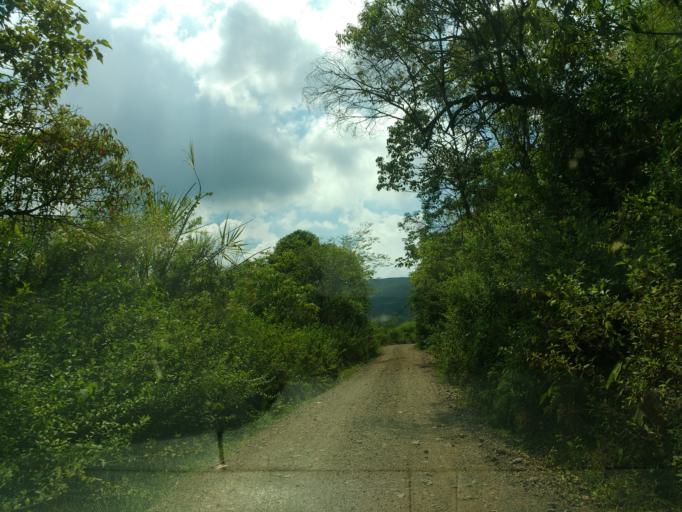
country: CO
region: Cauca
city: Buenos Aires
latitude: 3.1028
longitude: -76.6867
